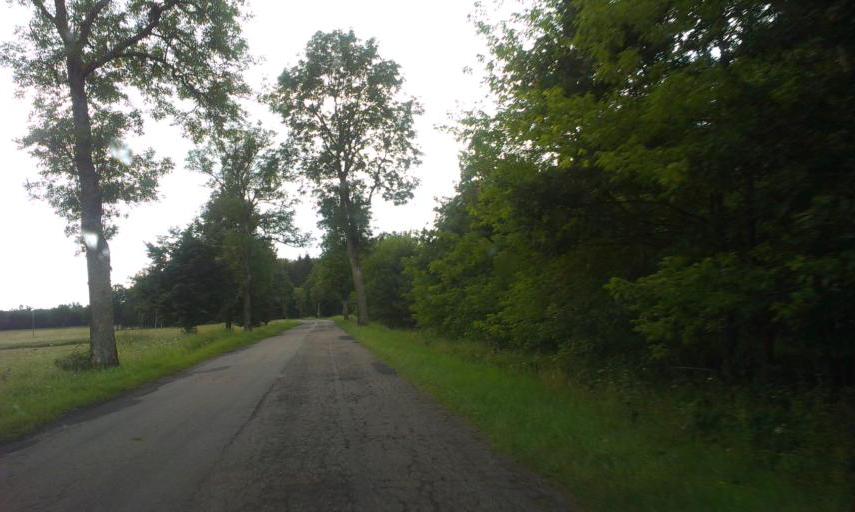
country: PL
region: West Pomeranian Voivodeship
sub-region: Powiat swidwinski
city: Polczyn-Zdroj
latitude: 53.8487
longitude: 16.1583
